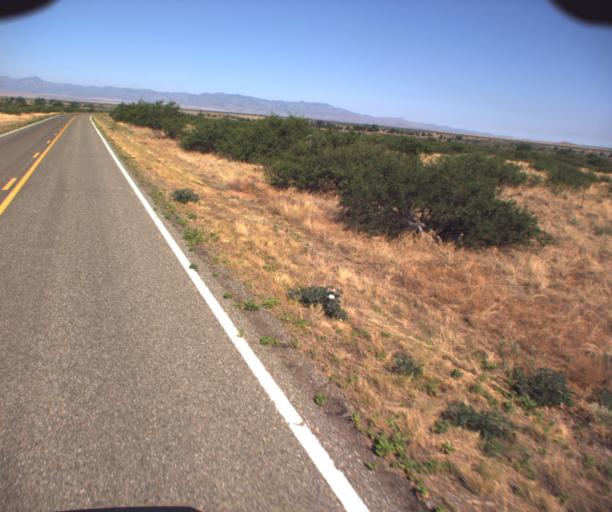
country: US
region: Arizona
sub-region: Graham County
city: Swift Trail Junction
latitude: 32.5827
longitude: -109.9464
